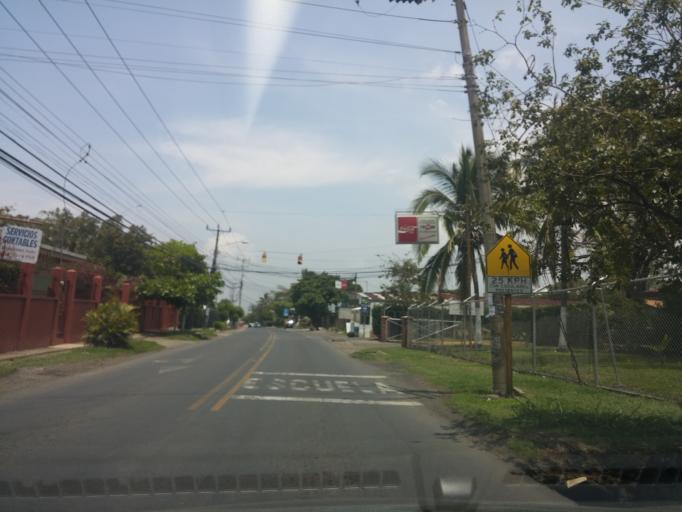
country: CR
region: Heredia
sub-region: Canton de Belen
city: San Antonio
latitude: 9.9777
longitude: -84.2036
